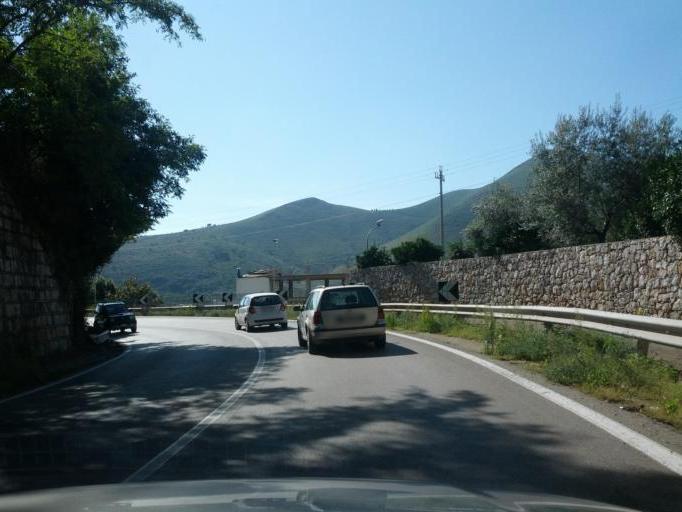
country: IT
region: Latium
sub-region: Provincia di Latina
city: Itri
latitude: 41.2667
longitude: 13.5501
